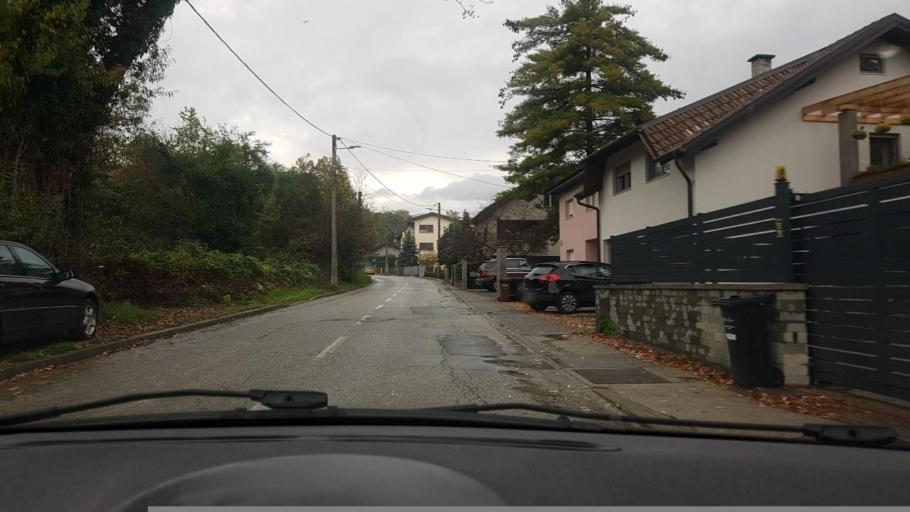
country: HR
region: Grad Zagreb
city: Zagreb
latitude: 45.8355
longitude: 16.0015
